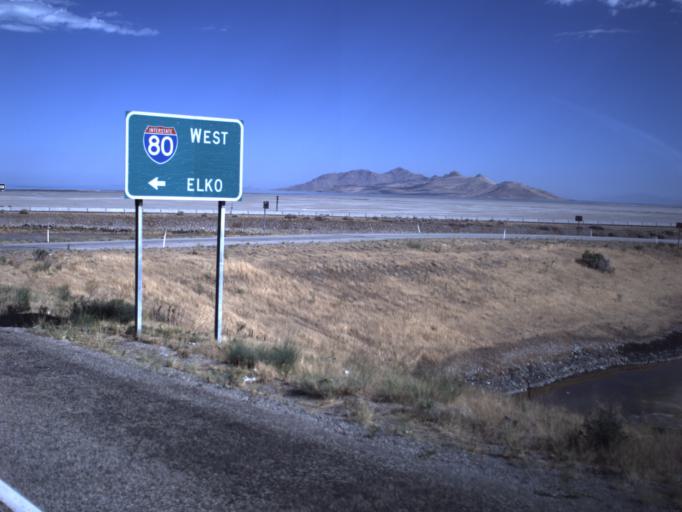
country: US
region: Utah
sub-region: Salt Lake County
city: Magna
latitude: 40.7459
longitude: -112.1840
